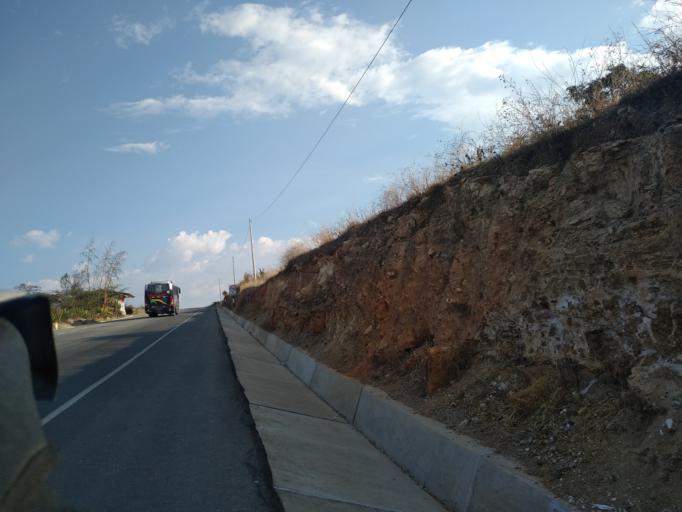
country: PE
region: Cajamarca
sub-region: San Marcos
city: La Grama
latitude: -7.4001
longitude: -78.1255
